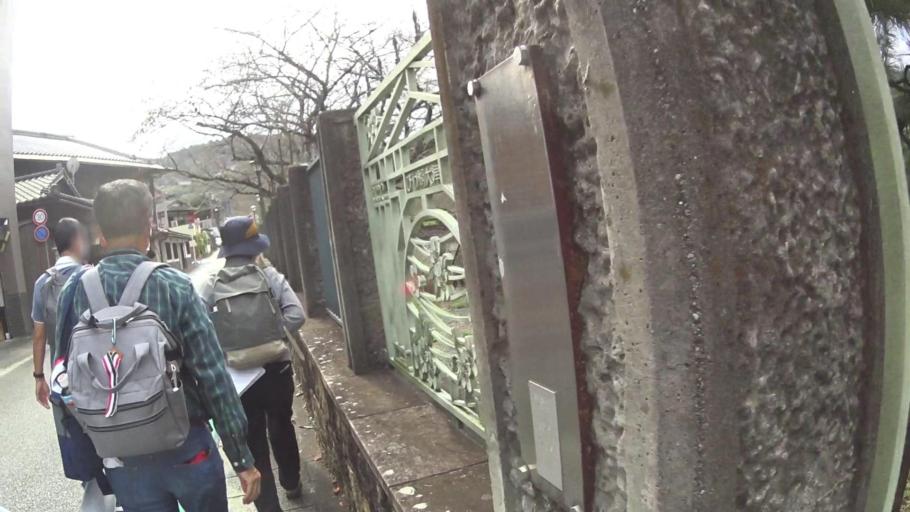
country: JP
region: Osaka
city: Kishiwada
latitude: 34.5136
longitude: 135.3461
